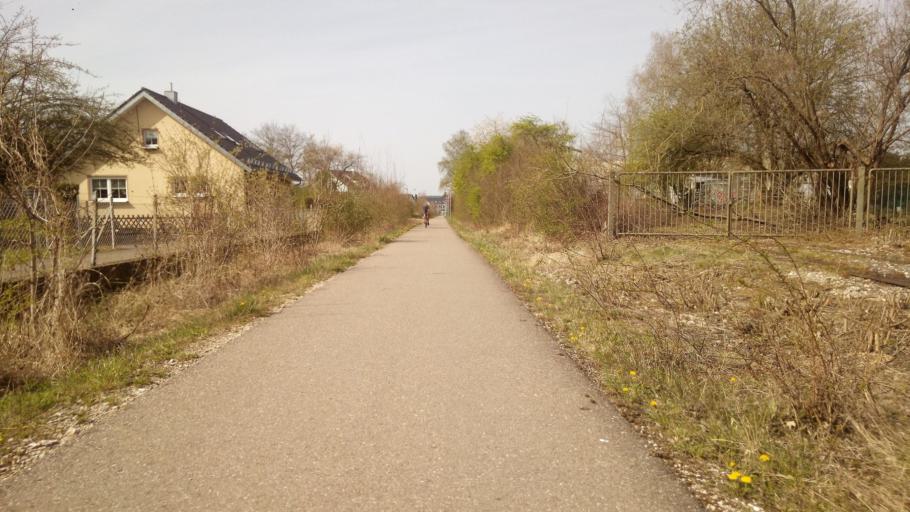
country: DE
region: Baden-Wuerttemberg
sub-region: Regierungsbezirk Stuttgart
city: Sussen
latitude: 48.6827
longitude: 9.7713
